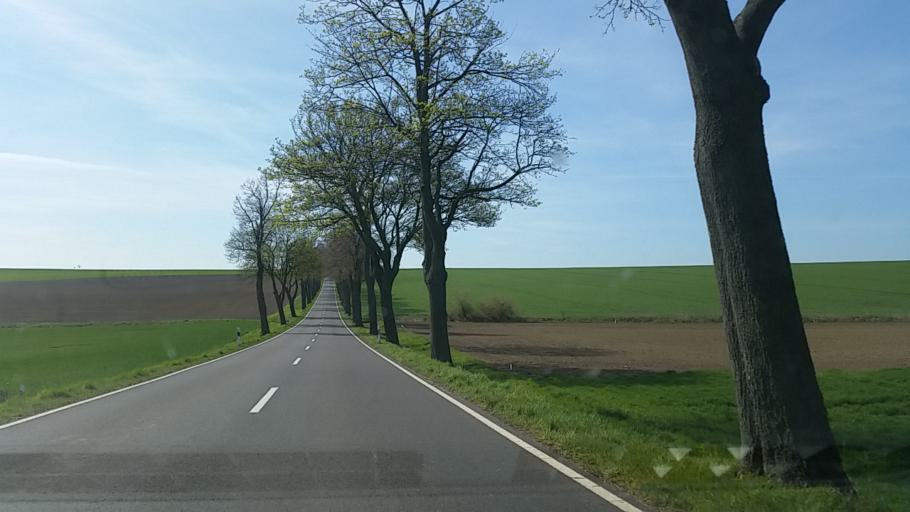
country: DE
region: Lower Saxony
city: Jerxheim
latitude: 52.0795
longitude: 10.8944
